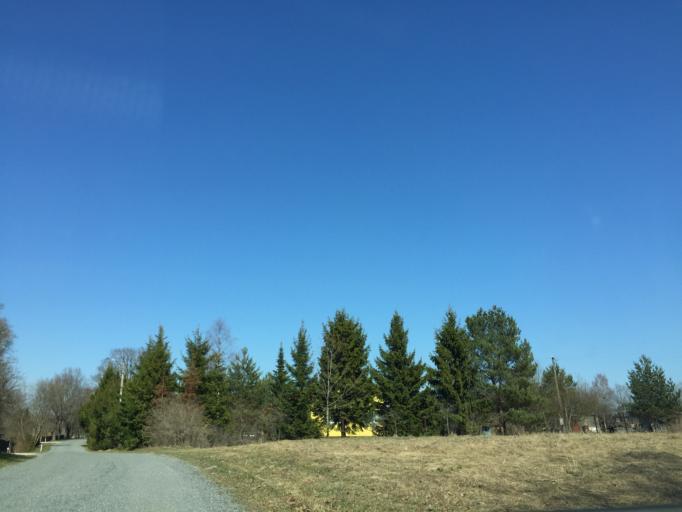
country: EE
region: Jogevamaa
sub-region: Mustvee linn
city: Mustvee
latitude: 58.9491
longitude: 27.0485
